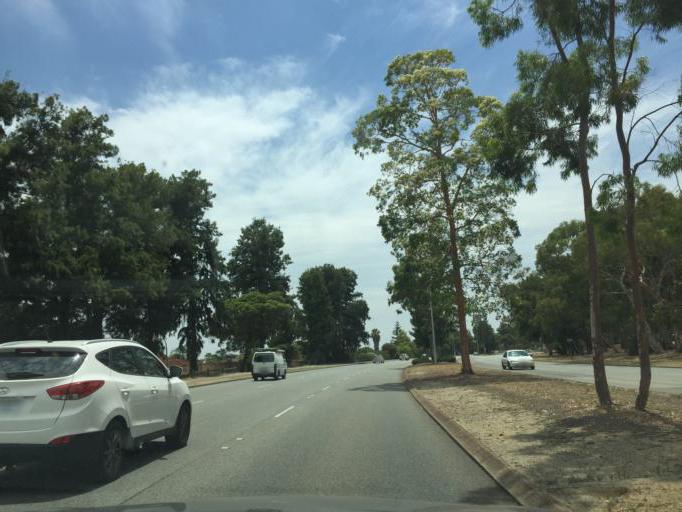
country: AU
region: Western Australia
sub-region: Melville
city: Winthrop
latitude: -32.0648
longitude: 115.8308
